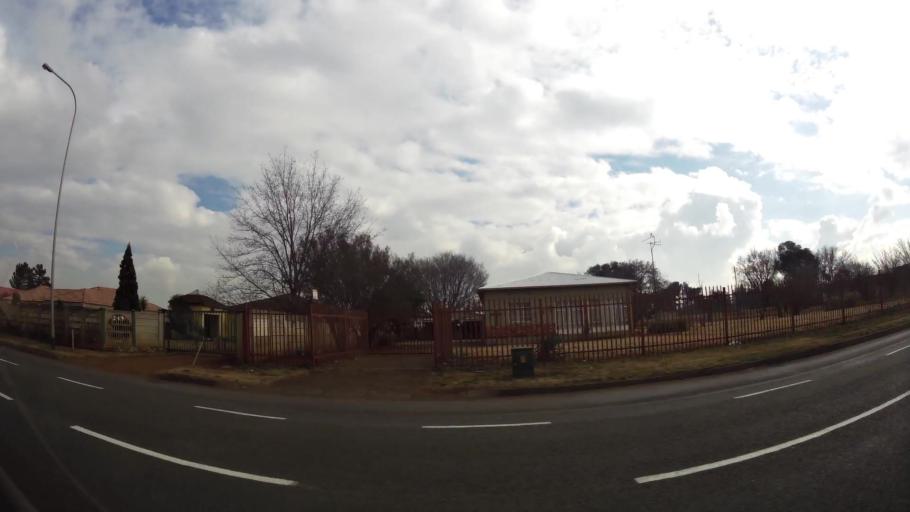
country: ZA
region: Gauteng
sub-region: Sedibeng District Municipality
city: Meyerton
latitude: -26.5947
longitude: 27.9935
